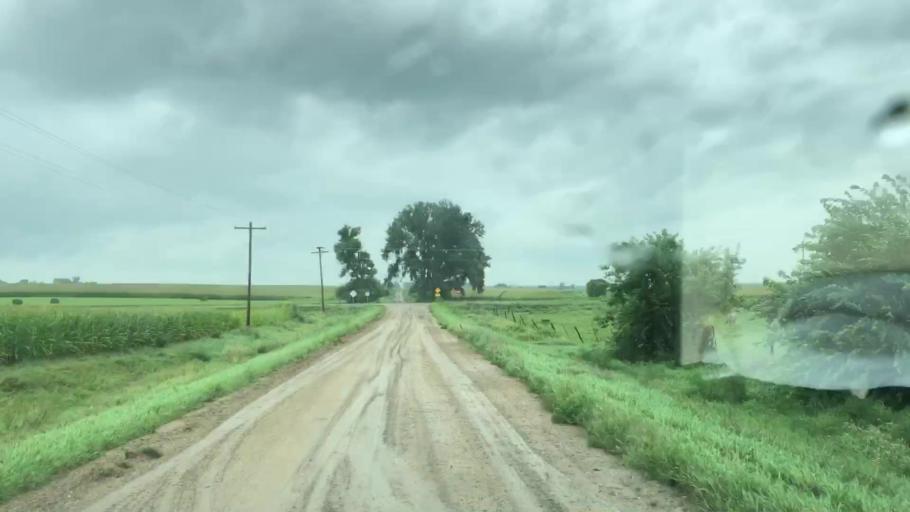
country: US
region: Iowa
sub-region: O'Brien County
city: Sanborn
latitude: 43.2741
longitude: -95.6841
